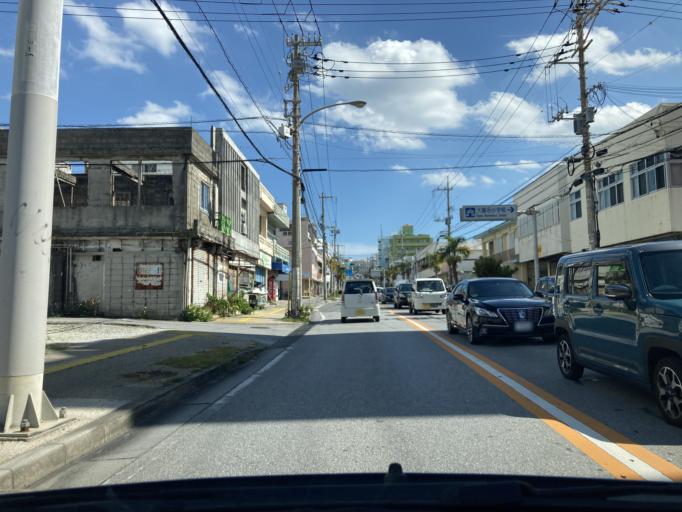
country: JP
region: Okinawa
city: Ginowan
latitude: 26.2683
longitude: 127.7338
